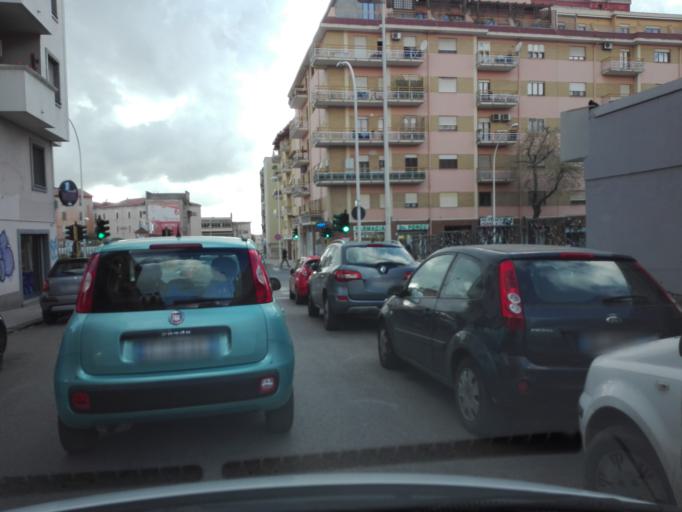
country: IT
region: Sardinia
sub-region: Provincia di Sassari
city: Sassari
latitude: 40.7353
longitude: 8.5613
